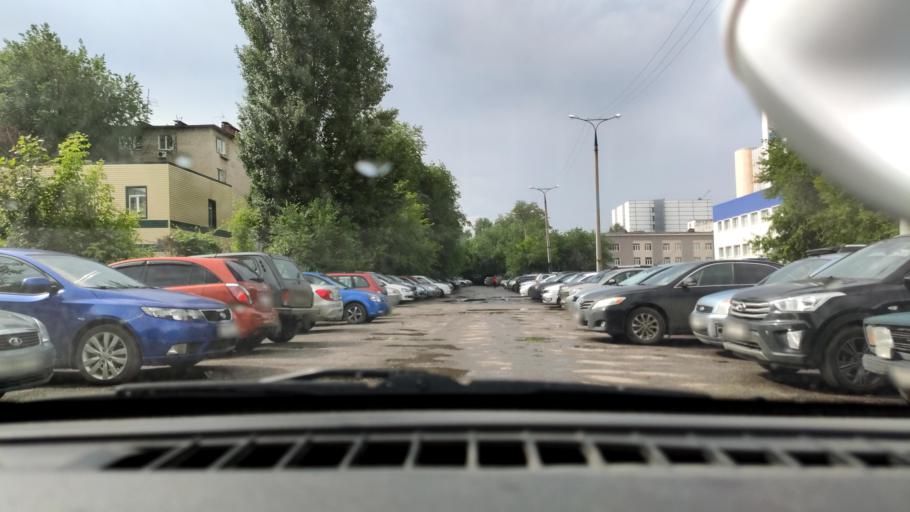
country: RU
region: Samara
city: Smyshlyayevka
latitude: 53.2136
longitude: 50.2978
